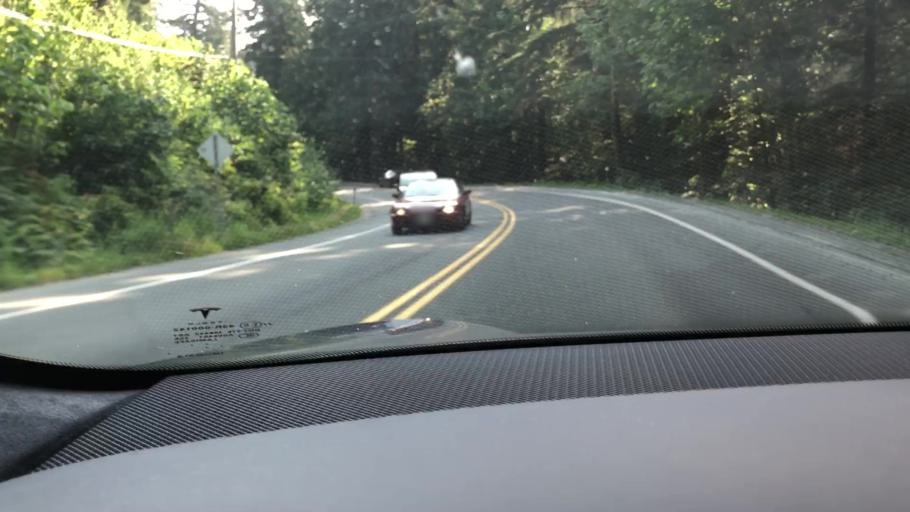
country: CA
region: British Columbia
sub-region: Fraser Valley Regional District
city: Chilliwack
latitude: 49.0815
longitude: -121.9781
